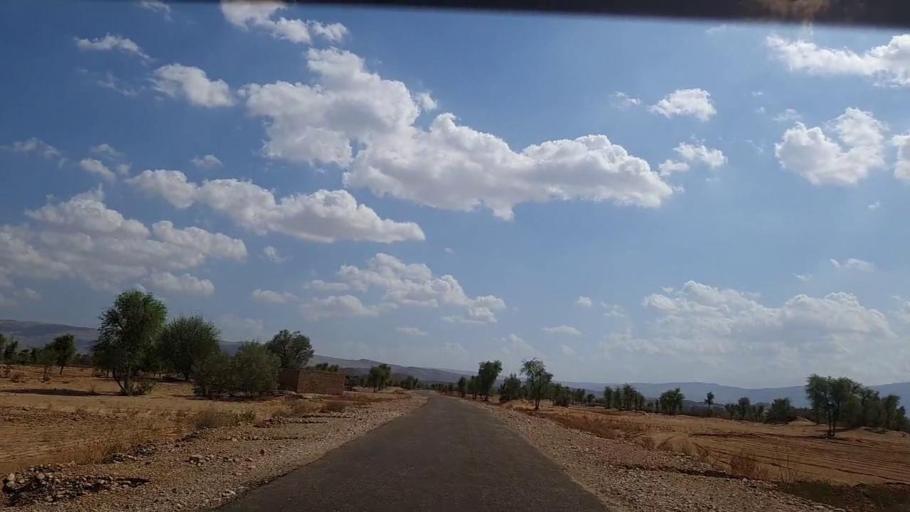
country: PK
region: Sindh
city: Johi
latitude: 26.5097
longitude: 67.4460
